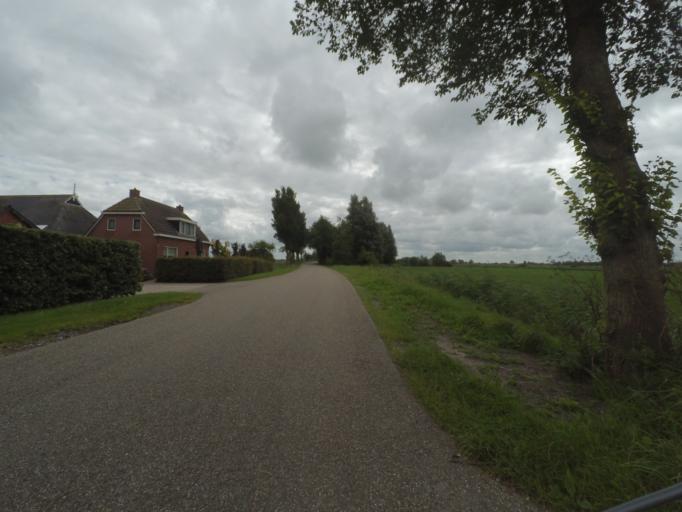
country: NL
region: Friesland
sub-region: Gemeente Kollumerland en Nieuwkruisland
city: Kollumerzwaag
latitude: 53.3079
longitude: 6.0893
